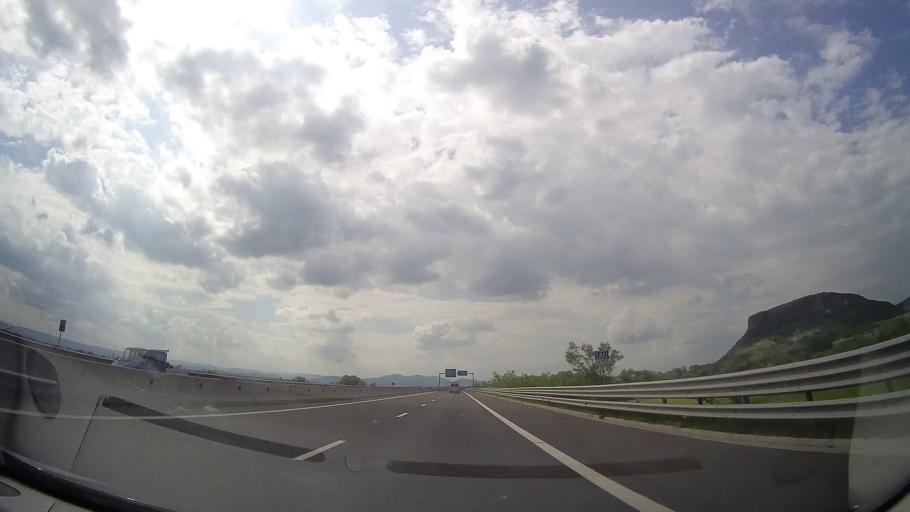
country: RO
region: Hunedoara
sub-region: Comuna Rapoltu Mare
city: Rapoltu Mare
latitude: 45.8479
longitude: 23.0547
